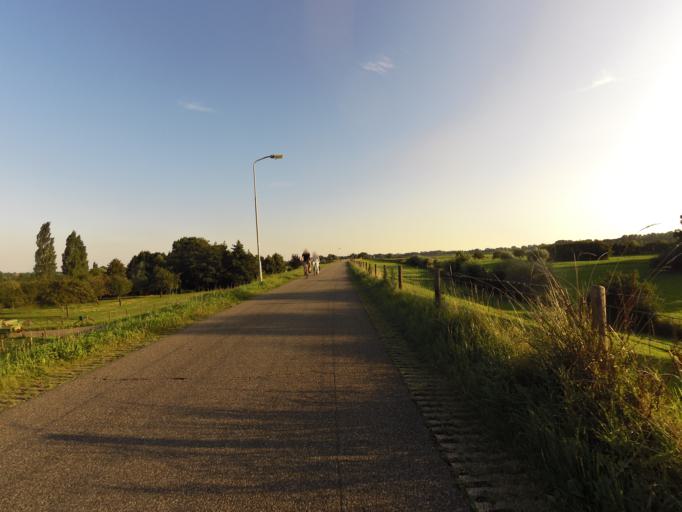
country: NL
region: Gelderland
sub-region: Gemeente Westervoort
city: Westervoort
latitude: 51.9381
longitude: 5.9692
